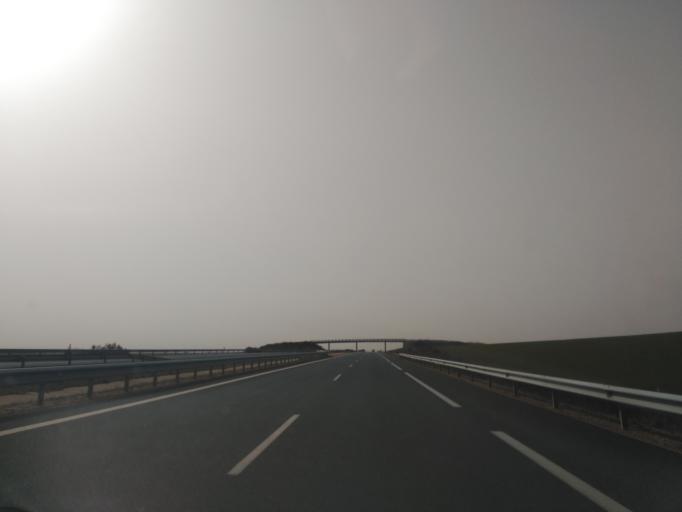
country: ES
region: Castille and Leon
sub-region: Provincia de Palencia
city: Espinosa de Villagonzalo
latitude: 42.4583
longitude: -4.3870
